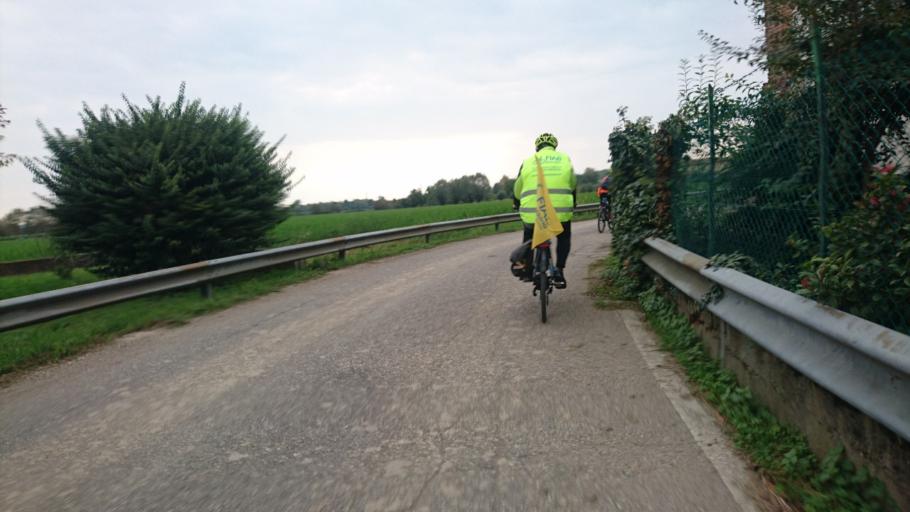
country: IT
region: Veneto
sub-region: Provincia di Verona
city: San Giovanni Lupatoto
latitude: 45.4079
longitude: 11.0588
